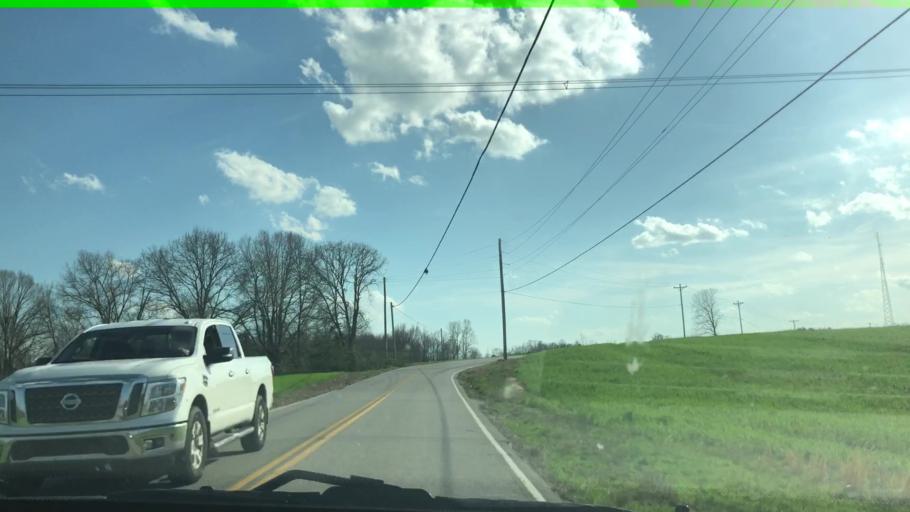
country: US
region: Tennessee
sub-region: Putnam County
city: Baxter
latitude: 36.0784
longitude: -85.5867
